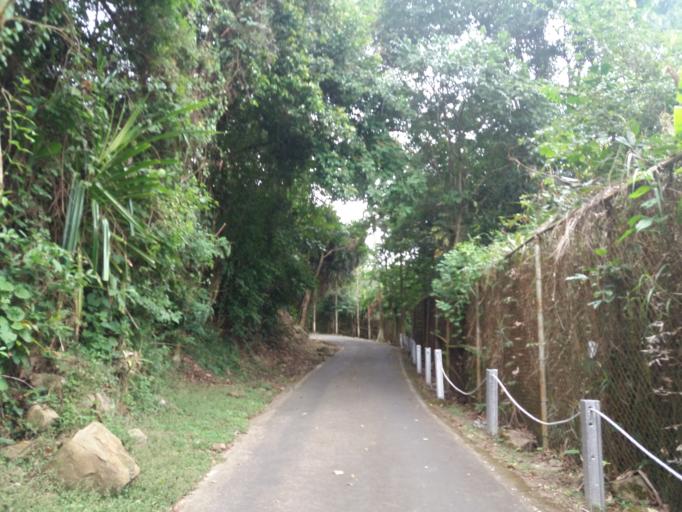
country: PA
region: Panama
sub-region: Distrito de Panama
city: Ancon
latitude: 8.9580
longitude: -79.5497
